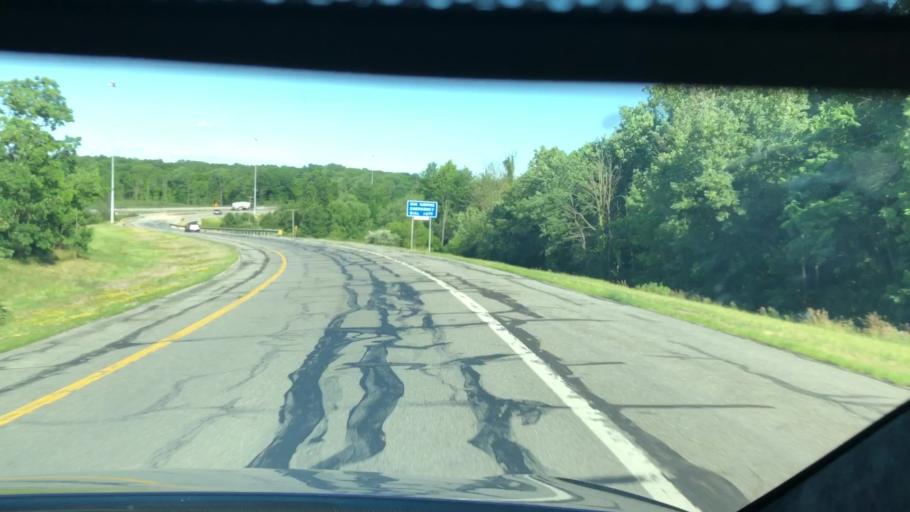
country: US
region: Ohio
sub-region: Mahoning County
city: Poland
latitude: 40.9522
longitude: -80.6385
